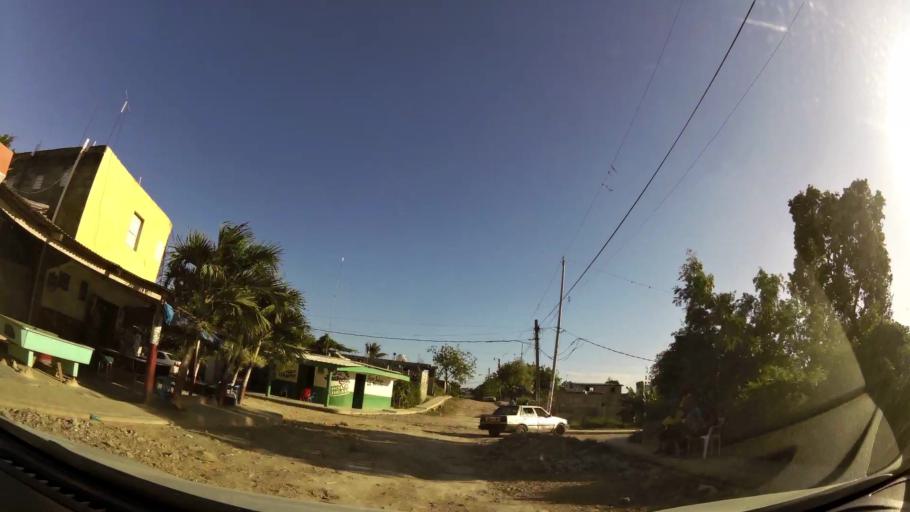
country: DO
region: Santo Domingo
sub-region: Santo Domingo
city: Santo Domingo Este
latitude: 18.4779
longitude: -69.8184
